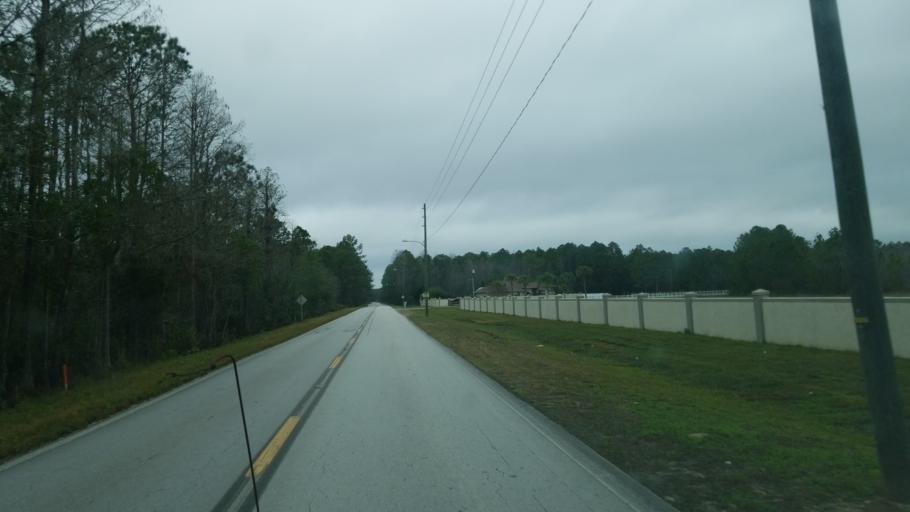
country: US
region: Florida
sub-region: Lake County
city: Four Corners
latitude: 28.2561
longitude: -81.6793
